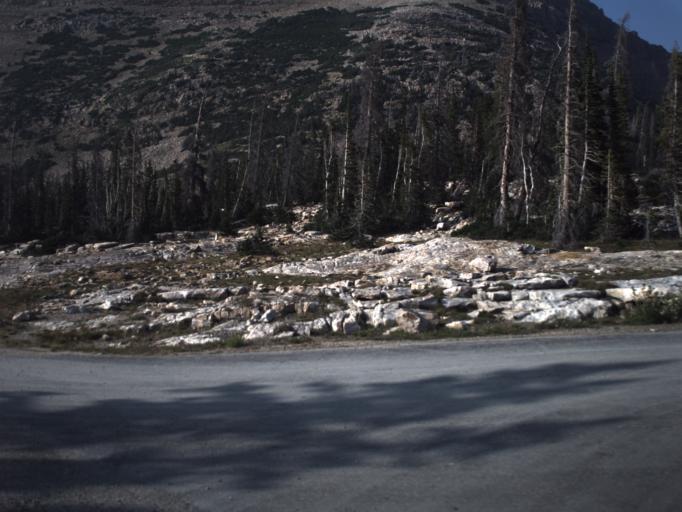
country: US
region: Utah
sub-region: Summit County
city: Kamas
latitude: 40.6873
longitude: -110.9044
